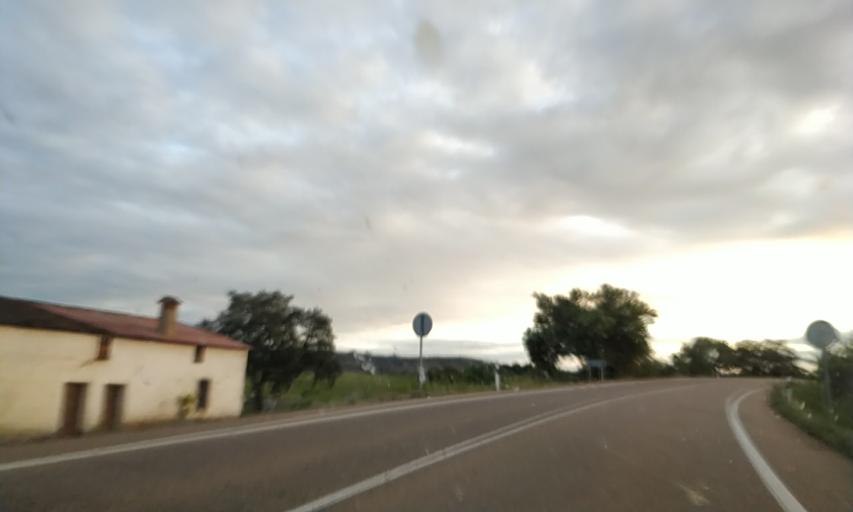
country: ES
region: Extremadura
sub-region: Provincia de Badajoz
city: Puebla de Obando
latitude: 39.1841
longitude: -6.6011
